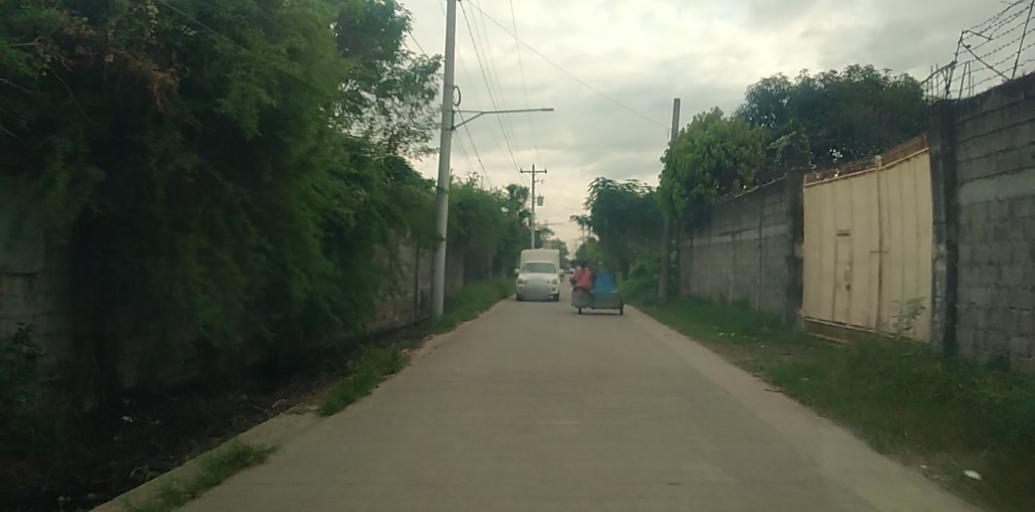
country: PH
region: Central Luzon
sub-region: Province of Pampanga
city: San Fernando
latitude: 15.0071
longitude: 120.7038
